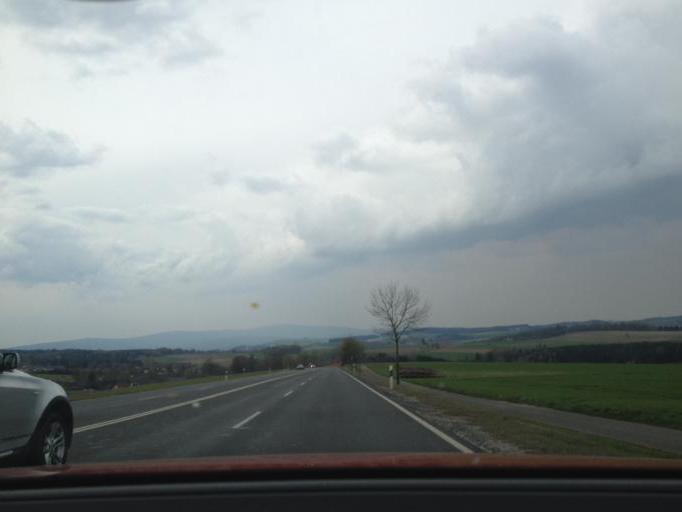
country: DE
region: Bavaria
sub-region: Upper Franconia
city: Bad Alexandersbad
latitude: 50.0181
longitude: 12.0388
